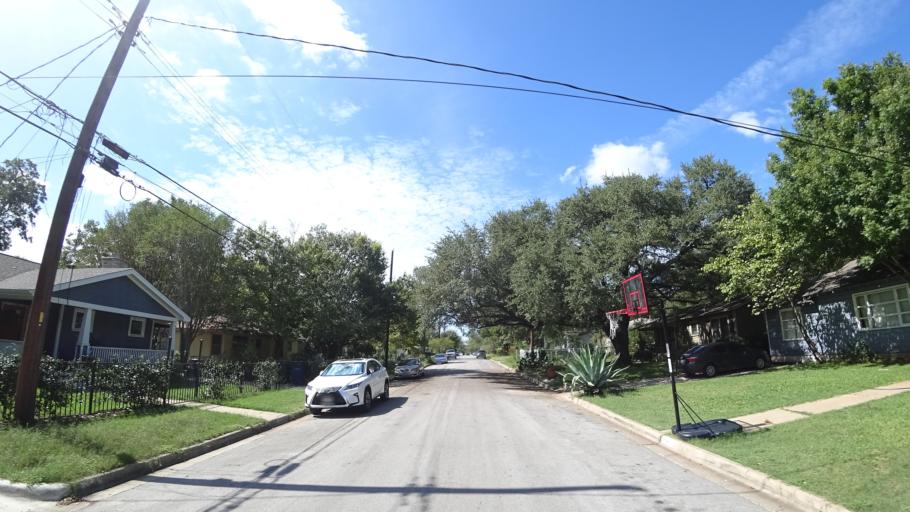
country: US
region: Texas
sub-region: Travis County
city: Austin
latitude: 30.3429
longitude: -97.7227
